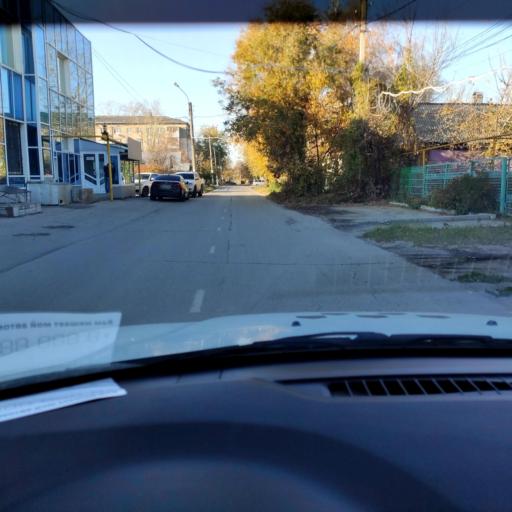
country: RU
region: Samara
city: Tol'yatti
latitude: 53.5197
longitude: 49.4115
